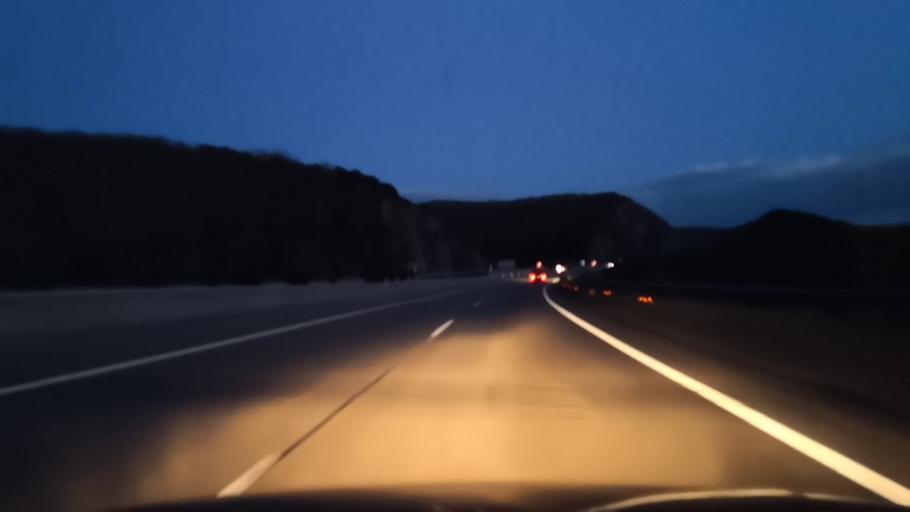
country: ES
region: Castille and Leon
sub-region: Provincia de Leon
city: Folgoso de la Ribera
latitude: 42.6205
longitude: -6.2818
